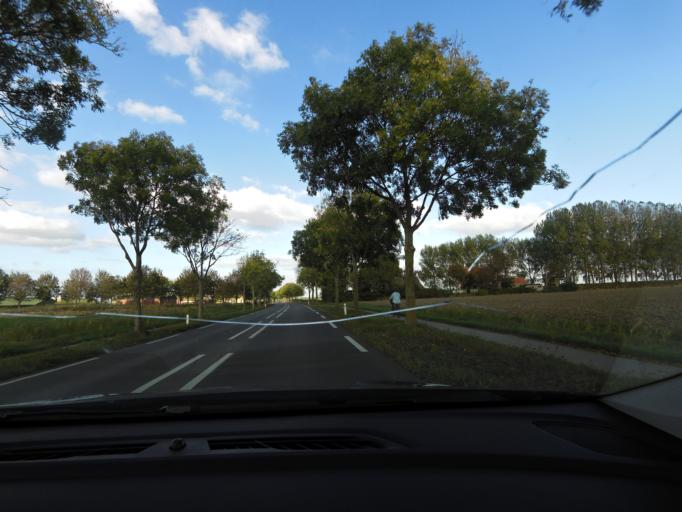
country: NL
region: North Brabant
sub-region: Gemeente Steenbergen
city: Dinteloord
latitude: 51.6100
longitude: 4.3506
